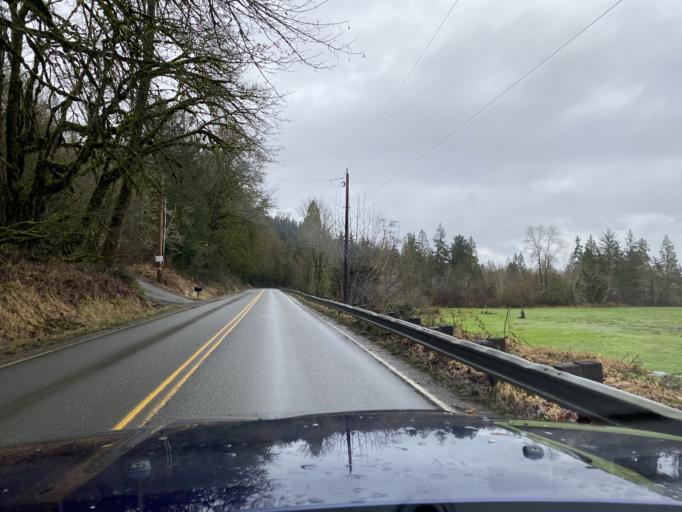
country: US
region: Washington
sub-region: King County
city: Duvall
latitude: 47.7530
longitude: -122.0045
